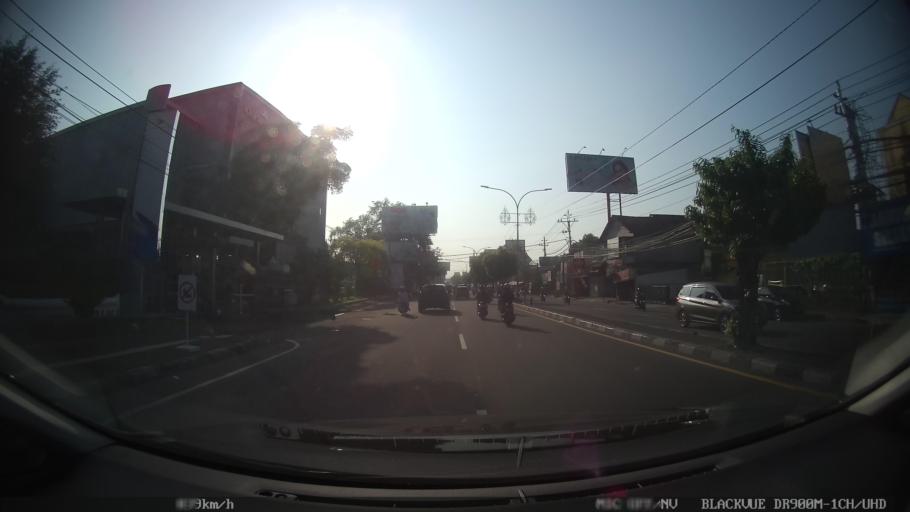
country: ID
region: Daerah Istimewa Yogyakarta
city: Depok
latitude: -7.7832
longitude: 110.4025
